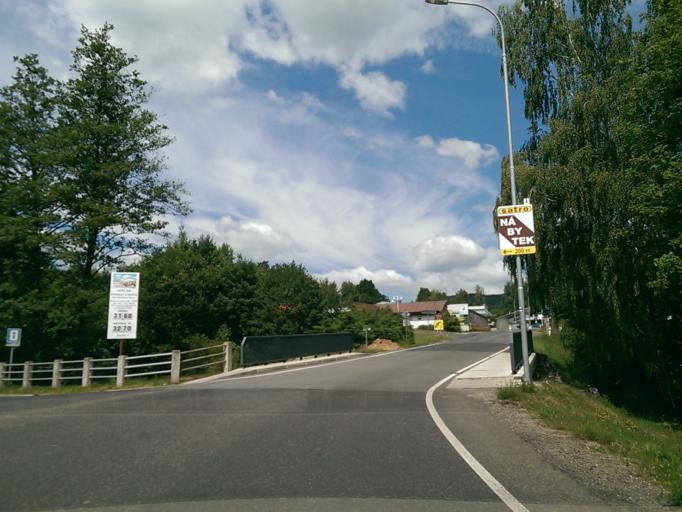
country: CZ
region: Liberecky
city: Semily
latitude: 50.6065
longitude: 15.3238
